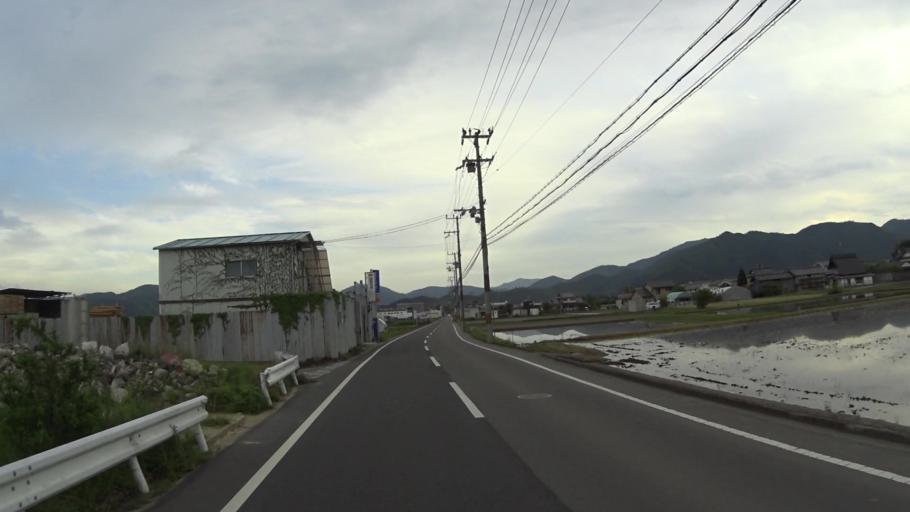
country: JP
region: Kyoto
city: Kameoka
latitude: 35.0262
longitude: 135.5431
